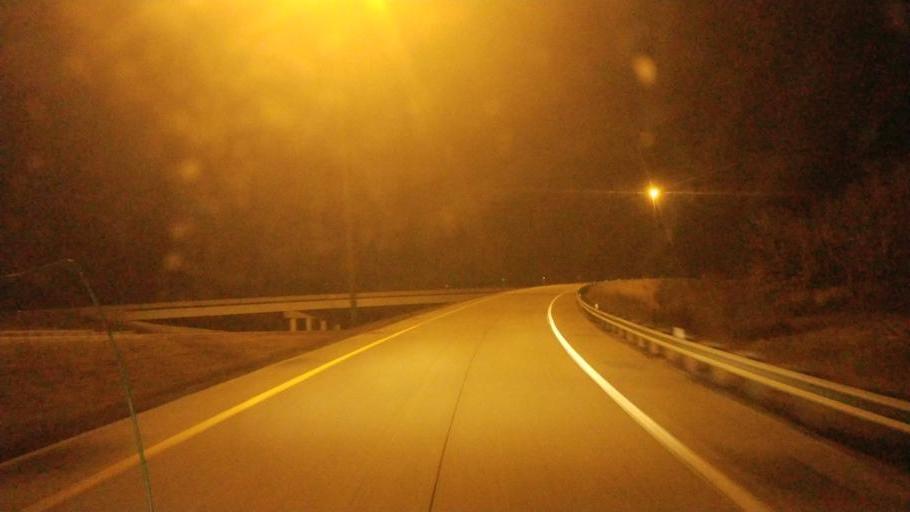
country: US
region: Missouri
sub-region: Howell County
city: Willow Springs
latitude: 36.9634
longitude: -91.9299
